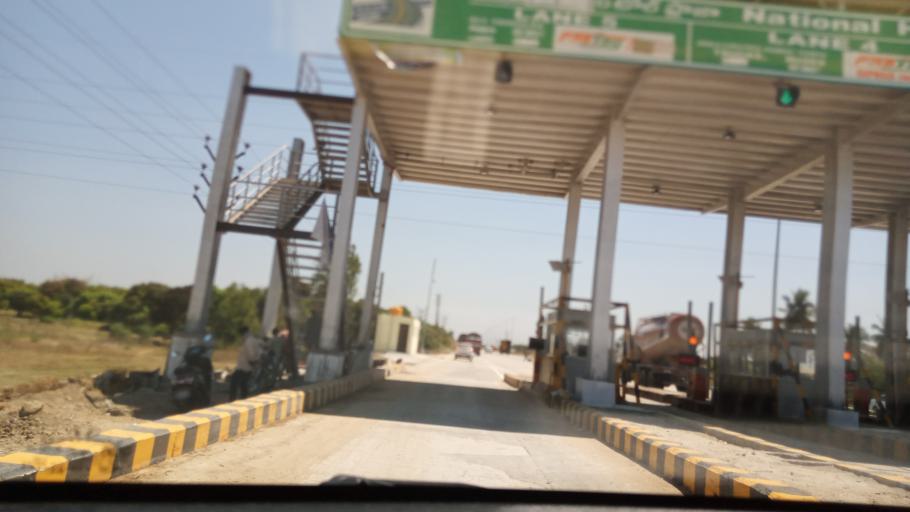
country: IN
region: Andhra Pradesh
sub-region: Chittoor
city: Chittoor
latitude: 13.1950
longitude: 79.0182
